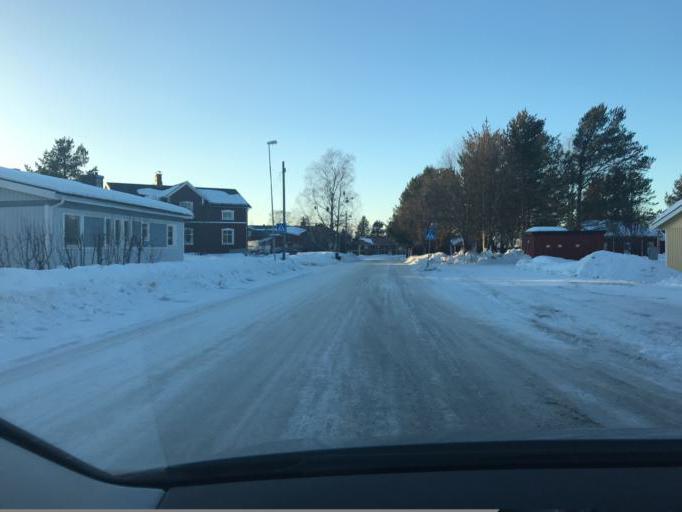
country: SE
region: Norrbotten
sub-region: Lulea Kommun
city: Sodra Sunderbyn
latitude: 65.6597
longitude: 21.9380
